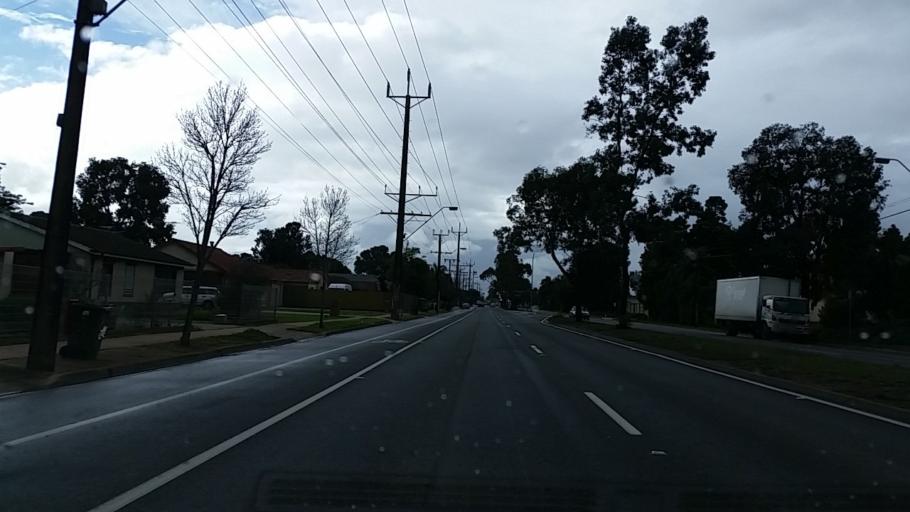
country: AU
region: South Australia
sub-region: Salisbury
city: Salisbury
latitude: -34.7825
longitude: 138.6234
